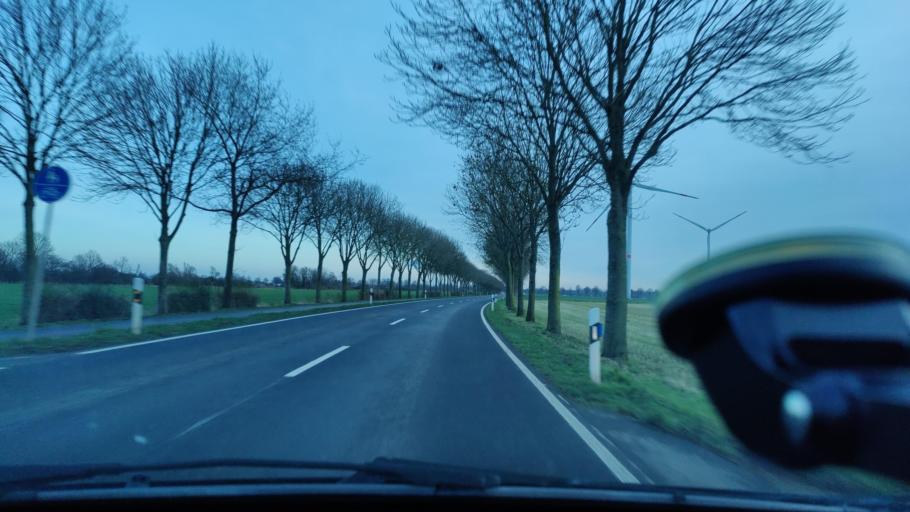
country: DE
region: North Rhine-Westphalia
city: Kalkar
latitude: 51.7505
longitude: 6.3166
